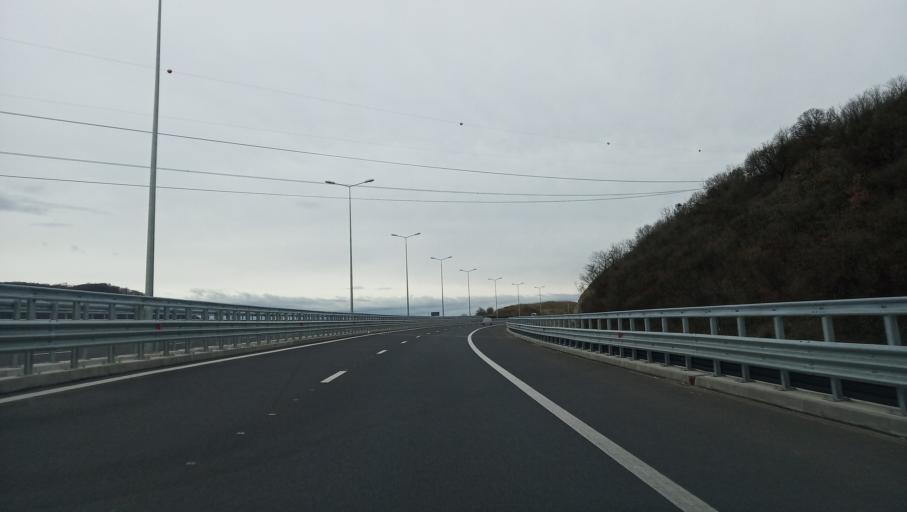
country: RO
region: Hunedoara
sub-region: Comuna Branisca
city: Branisca
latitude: 45.9115
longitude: 22.7888
